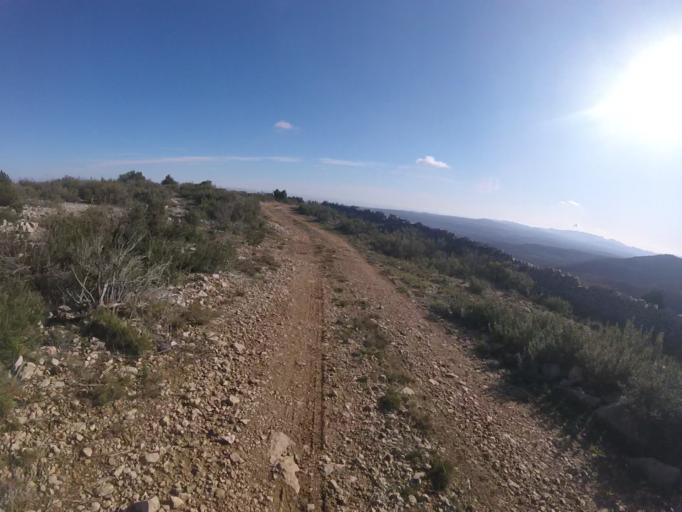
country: ES
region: Valencia
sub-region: Provincia de Castello
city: Sarratella
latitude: 40.3002
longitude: 0.0421
